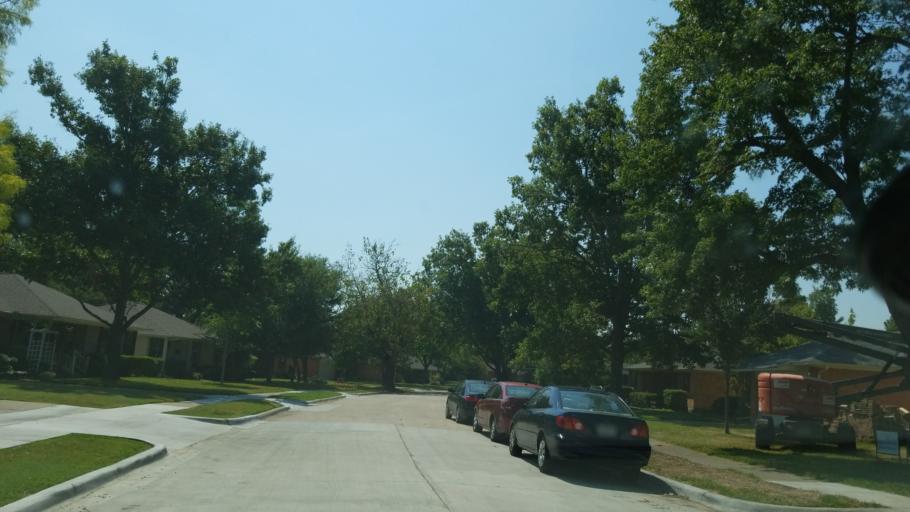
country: US
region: Texas
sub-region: Dallas County
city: Garland
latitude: 32.8729
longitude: -96.7056
